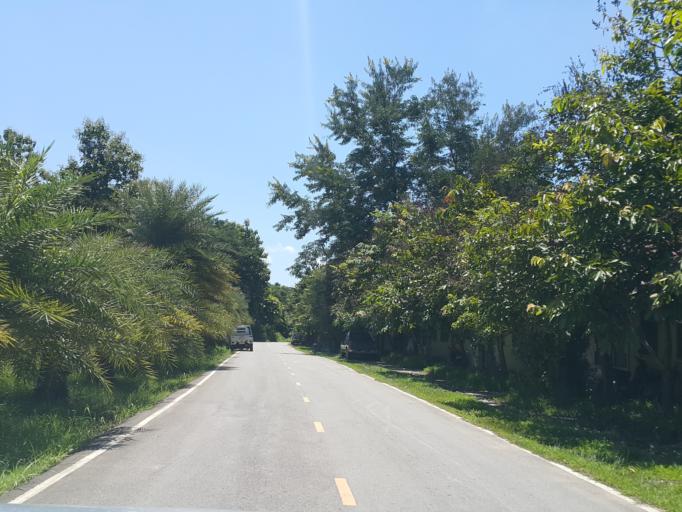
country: TH
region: Lamphun
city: Ban Thi
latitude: 18.6857
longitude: 99.1713
